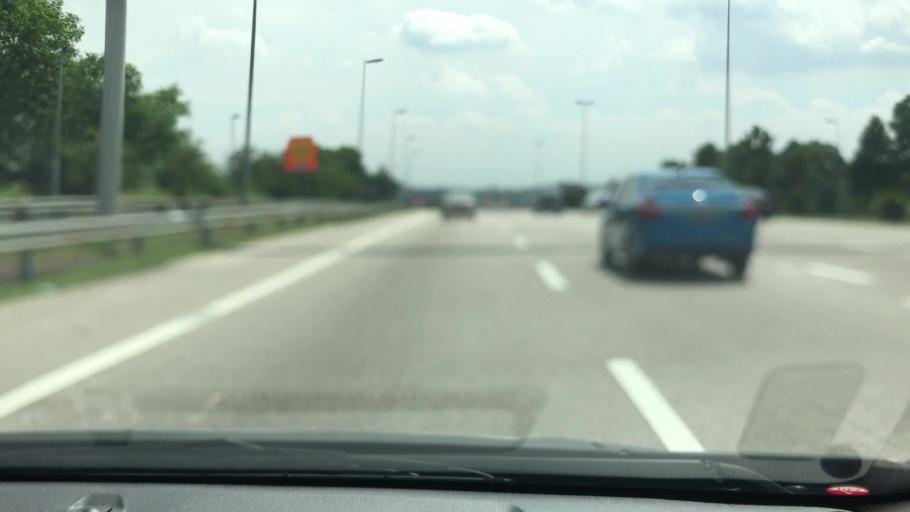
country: MY
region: Putrajaya
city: Putrajaya
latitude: 2.9790
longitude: 101.6610
